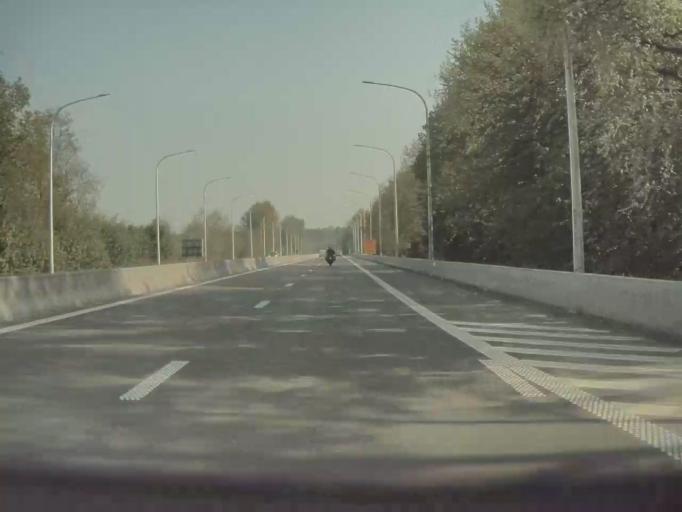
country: BE
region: Wallonia
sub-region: Province de Namur
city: Hamois
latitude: 50.2964
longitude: 5.1716
